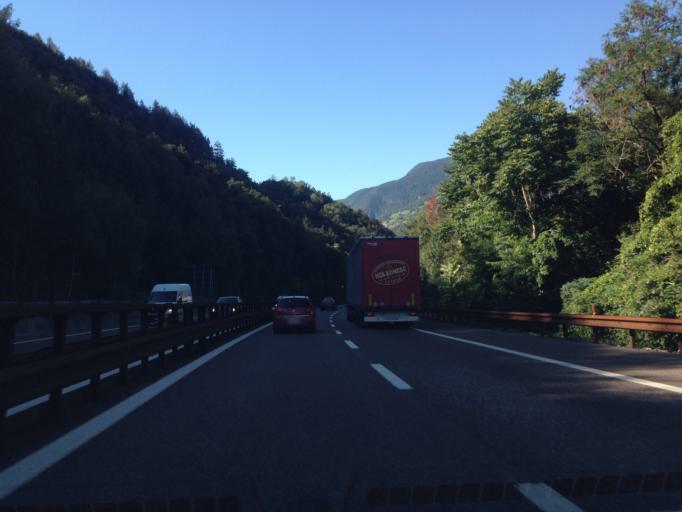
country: IT
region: Trentino-Alto Adige
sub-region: Bolzano
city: Chiusa
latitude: 46.6327
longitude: 11.5570
